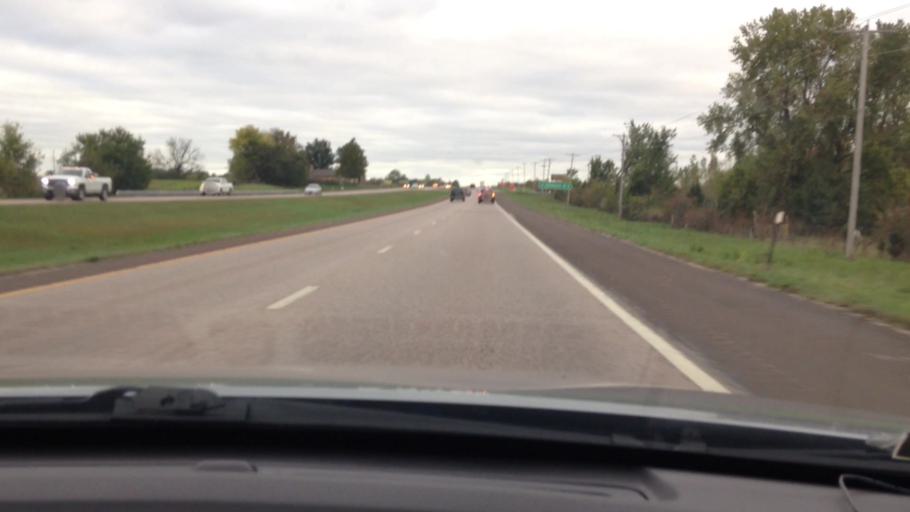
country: US
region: Kansas
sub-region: Leavenworth County
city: Basehor
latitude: 39.1751
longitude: -94.9007
